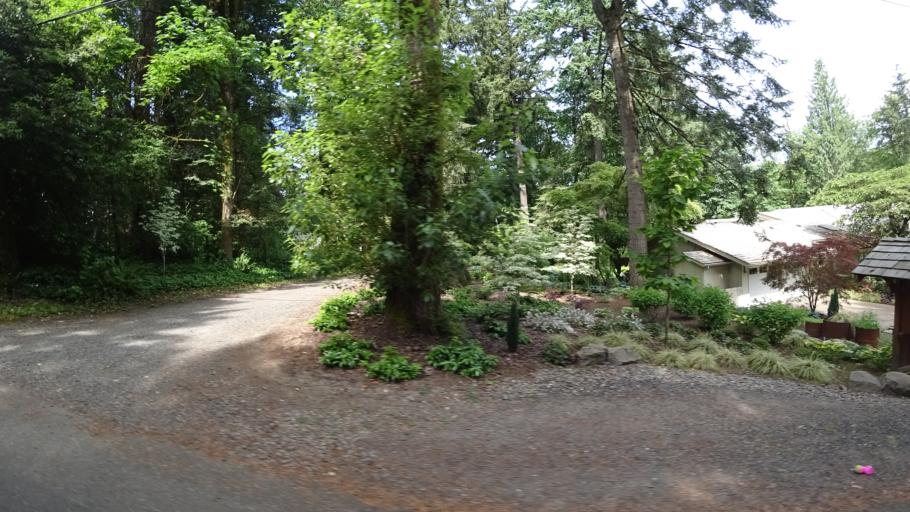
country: US
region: Oregon
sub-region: Clackamas County
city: Lake Oswego
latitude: 45.4510
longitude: -122.6750
